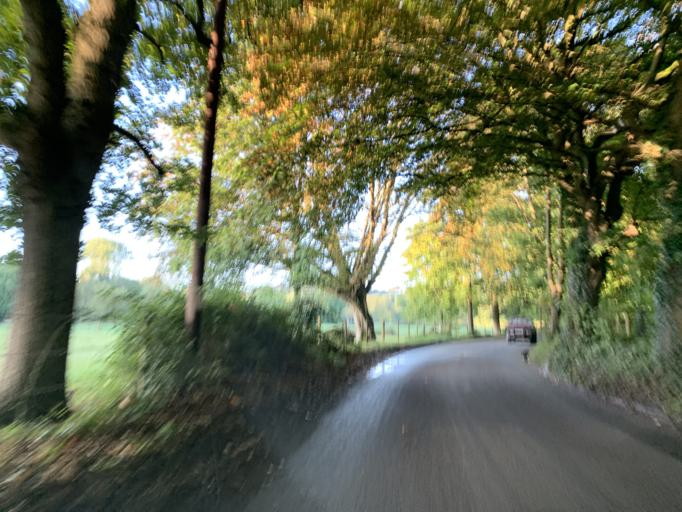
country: GB
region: England
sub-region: Wiltshire
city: Woodford
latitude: 51.1120
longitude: -1.8247
